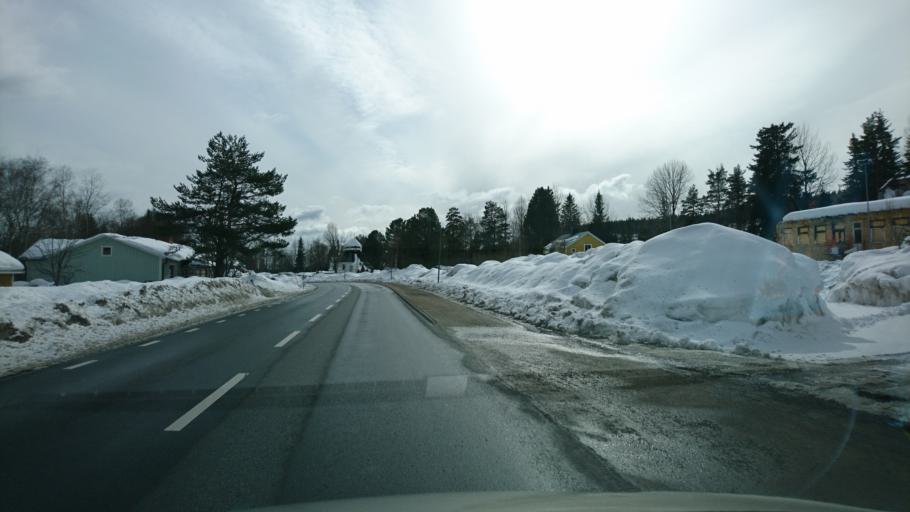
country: SE
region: Vaesternorrland
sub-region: Timra Kommun
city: Bergeforsen
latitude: 62.7709
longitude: 17.4197
